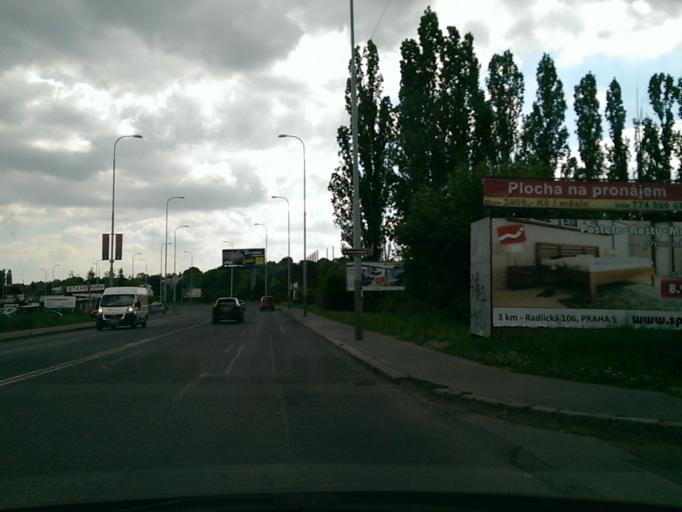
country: CZ
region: Praha
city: Branik
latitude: 50.0489
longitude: 14.3594
